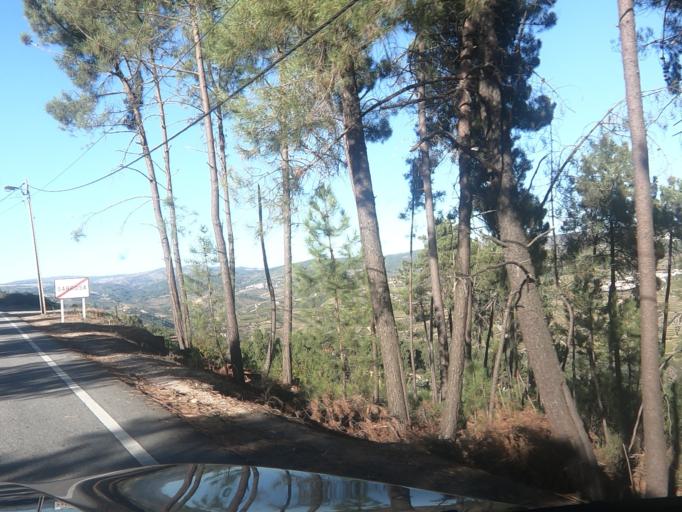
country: PT
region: Vila Real
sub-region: Sabrosa
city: Sabrosa
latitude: 41.2706
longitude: -7.5680
